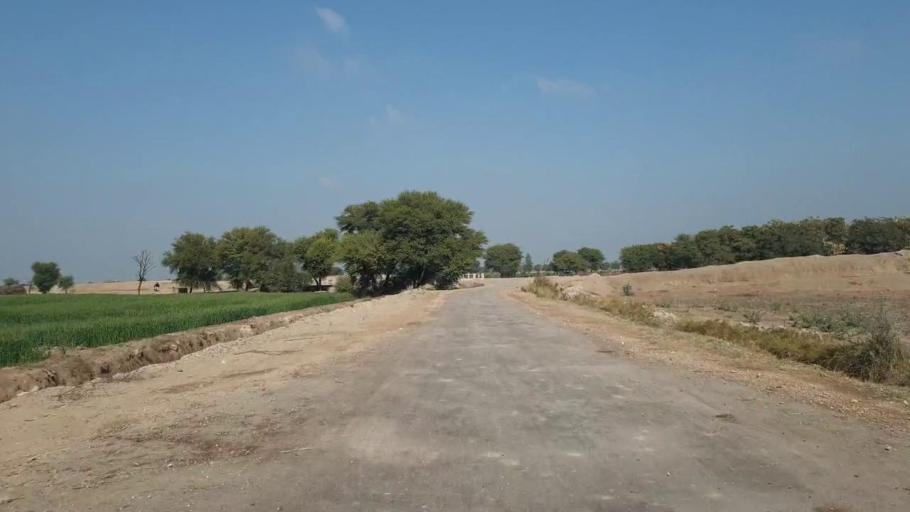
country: PK
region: Sindh
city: Shahdadpur
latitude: 26.0287
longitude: 68.6156
